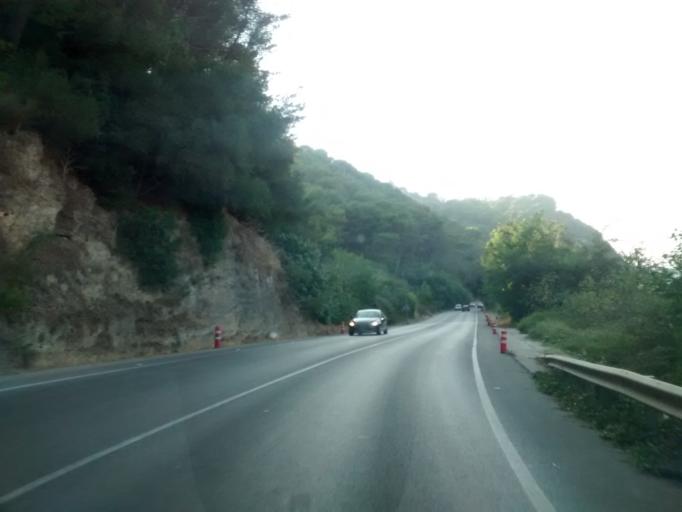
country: ES
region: Andalusia
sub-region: Provincia de Cadiz
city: Vejer de la Frontera
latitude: 36.2498
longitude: -5.9528
